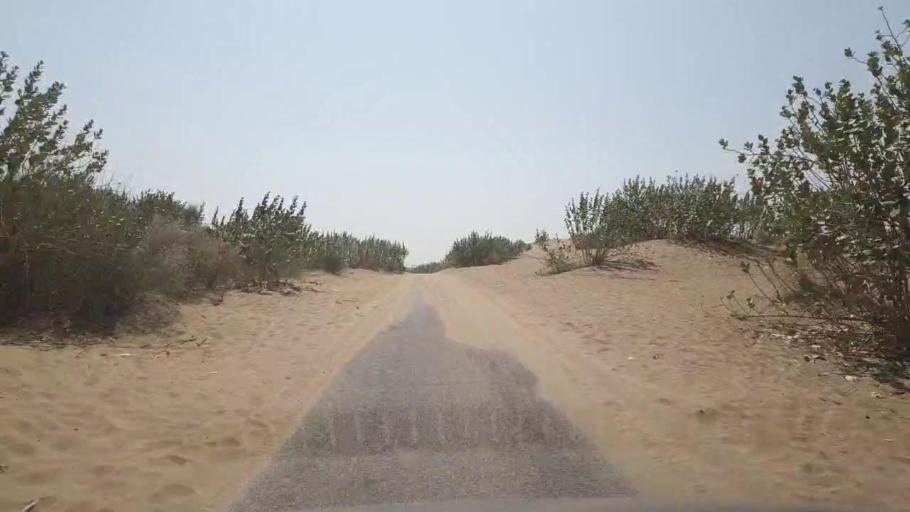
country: PK
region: Sindh
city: Chor
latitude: 25.6532
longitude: 70.1674
